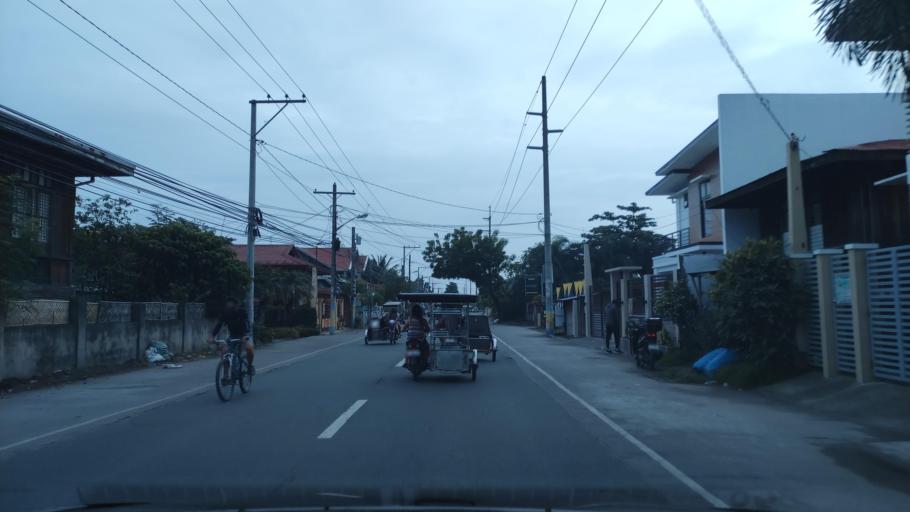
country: PH
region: Central Luzon
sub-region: Province of Pampanga
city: Santa Ana
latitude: 15.1084
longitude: 120.7717
